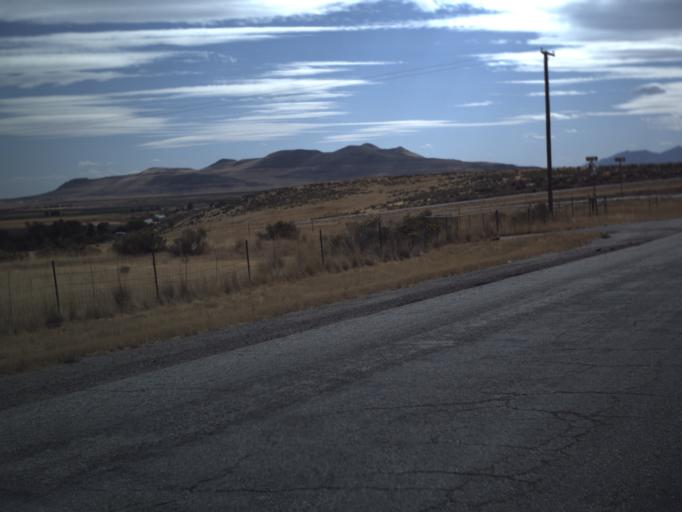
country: US
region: Utah
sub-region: Box Elder County
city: Tremonton
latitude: 41.7220
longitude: -112.2273
